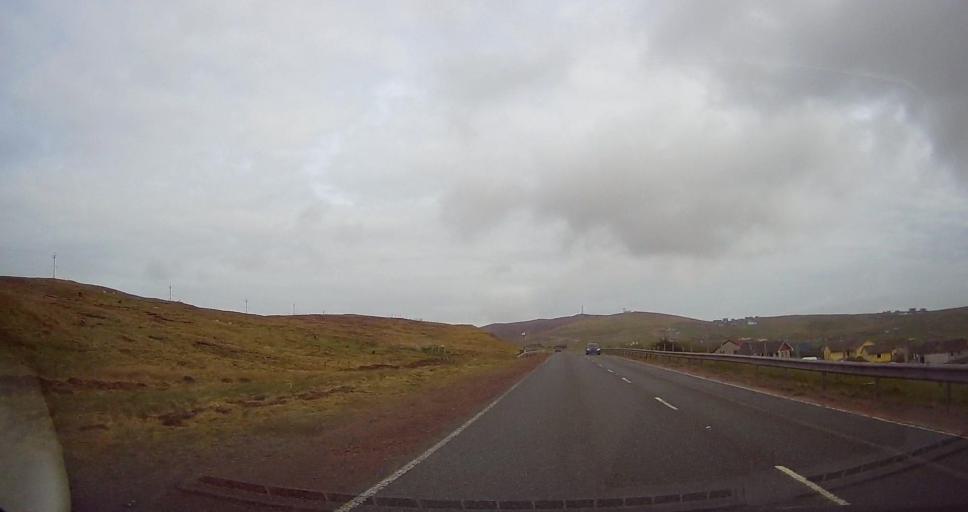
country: GB
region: Scotland
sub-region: Shetland Islands
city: Lerwick
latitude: 60.1262
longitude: -1.2173
